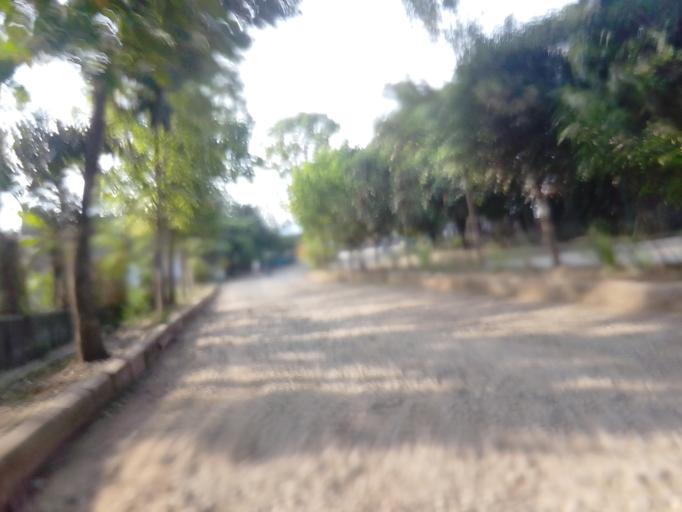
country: ID
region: West Java
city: Cileunyi
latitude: -6.9324
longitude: 107.7133
